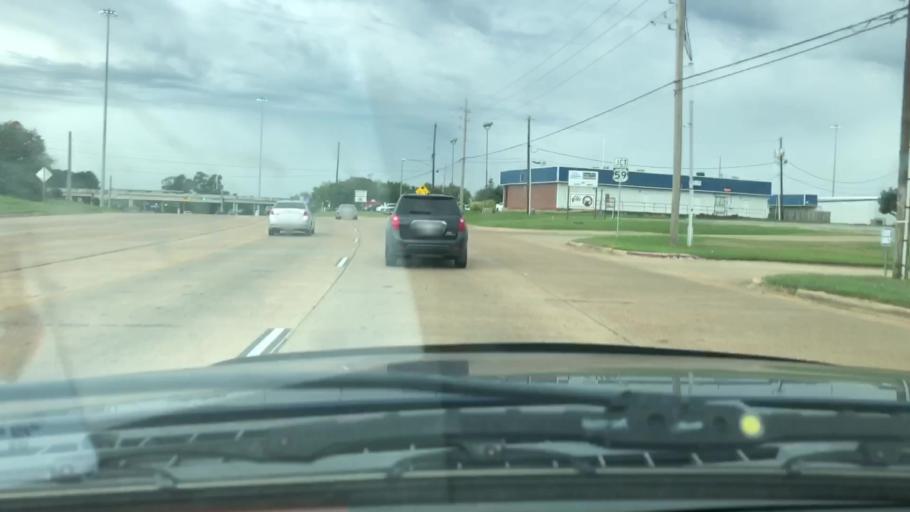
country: US
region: Texas
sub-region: Bowie County
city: Wake Village
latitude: 33.4431
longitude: -94.0938
